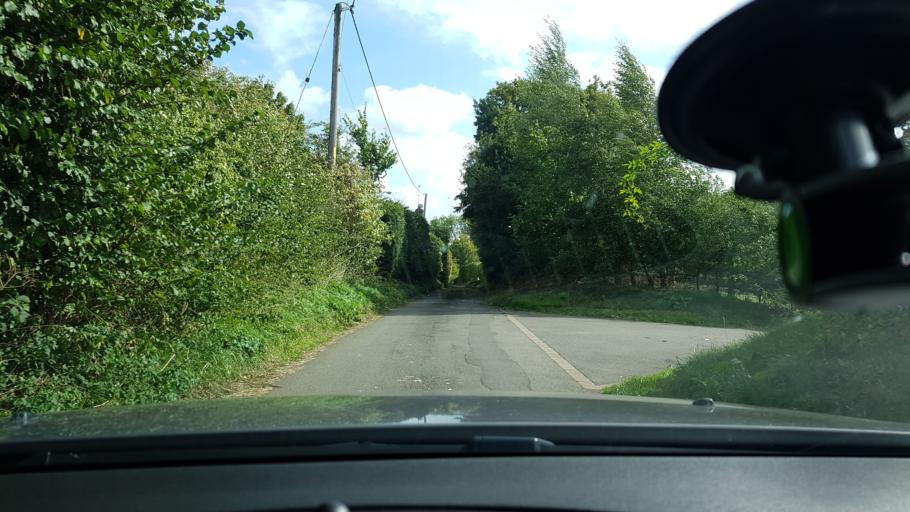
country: GB
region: England
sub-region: West Berkshire
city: Hungerford
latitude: 51.4580
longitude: -1.5019
